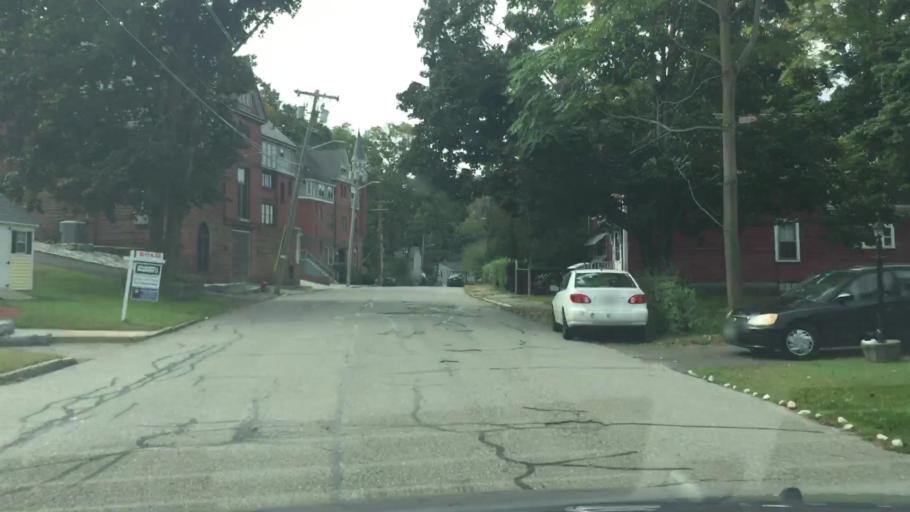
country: US
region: Massachusetts
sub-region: Middlesex County
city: Lowell
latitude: 42.6439
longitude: -71.2903
